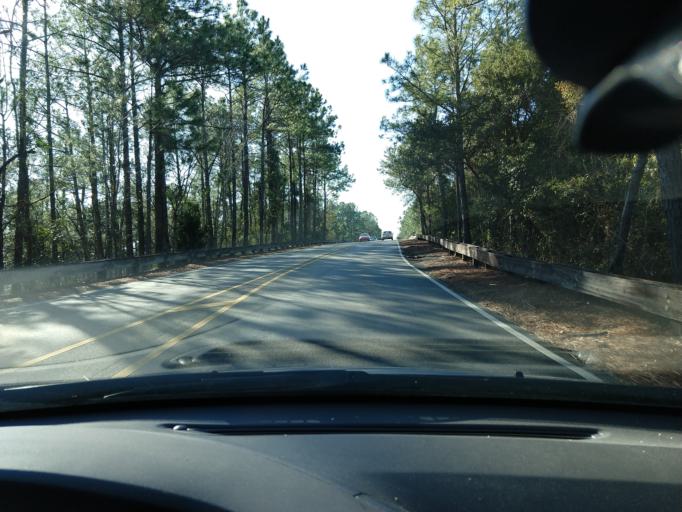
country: US
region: Mississippi
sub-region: Jackson County
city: Gulf Park Estates
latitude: 30.4106
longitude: -88.7793
